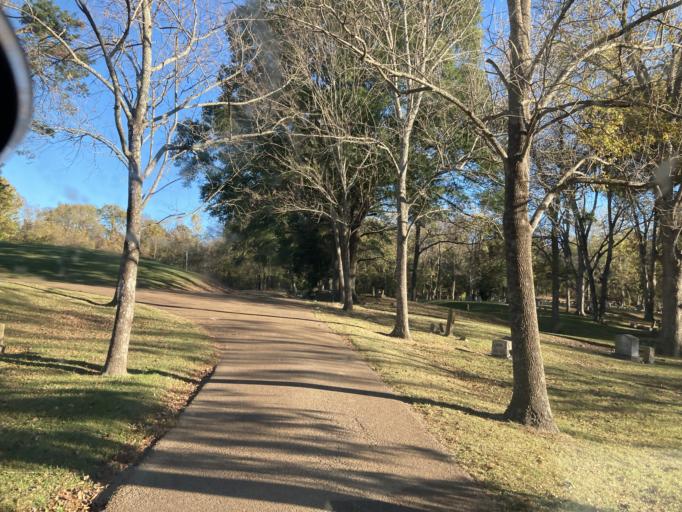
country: US
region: Mississippi
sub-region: Yazoo County
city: Yazoo City
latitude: 32.8500
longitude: -90.3985
